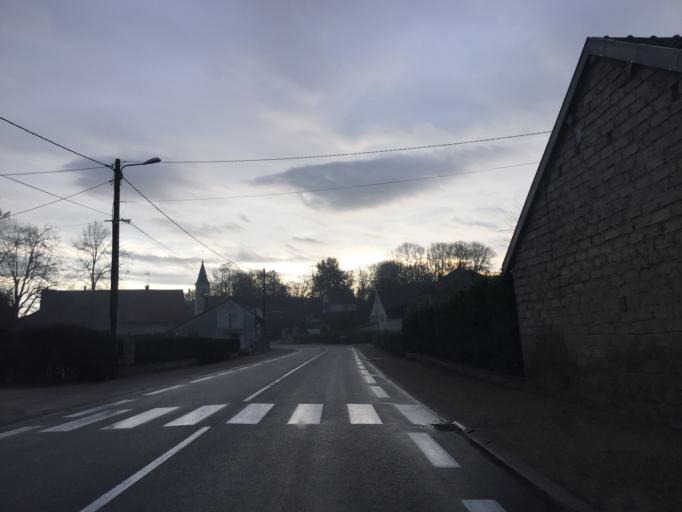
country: FR
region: Franche-Comte
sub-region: Departement du Jura
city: Choisey
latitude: 47.0031
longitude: 5.5159
